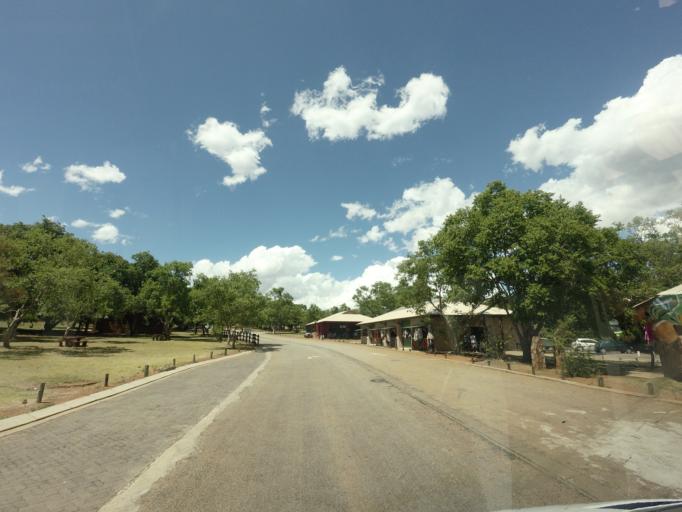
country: ZA
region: Mpumalanga
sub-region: Ehlanzeni District
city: Graksop
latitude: -24.6726
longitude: 30.8080
